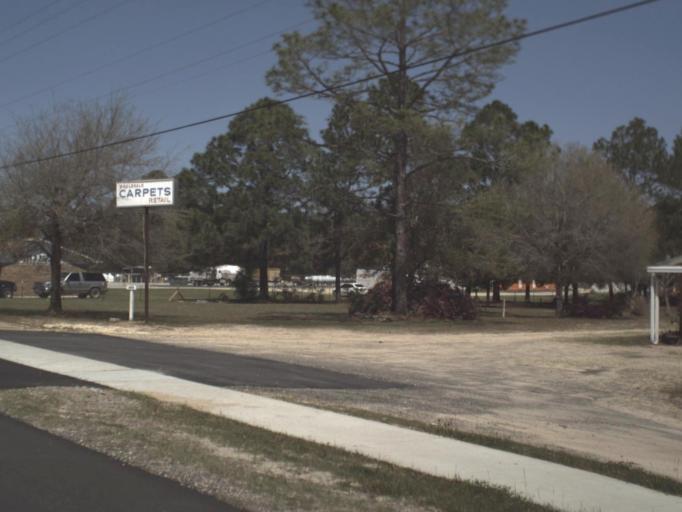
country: US
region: Florida
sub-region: Walton County
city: DeFuniak Springs
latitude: 30.7319
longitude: -86.1413
